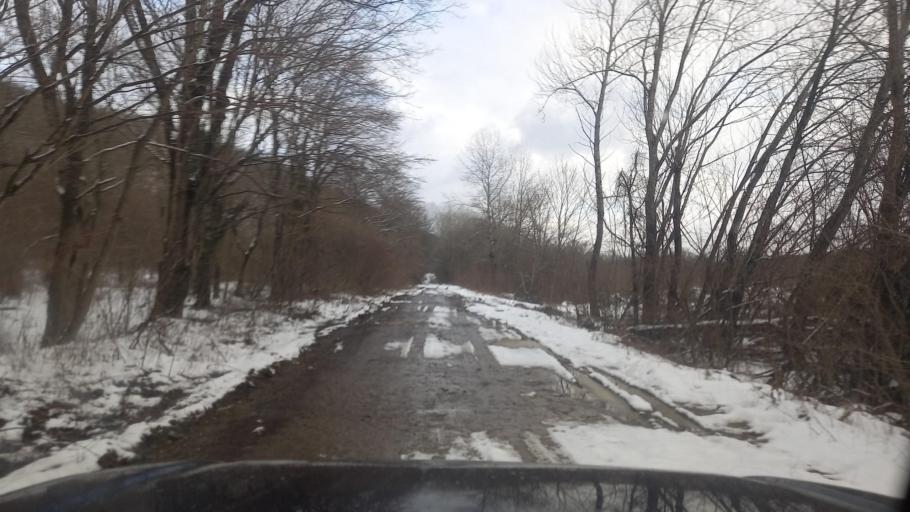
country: RU
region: Krasnodarskiy
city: Smolenskaya
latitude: 44.6899
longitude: 38.8578
